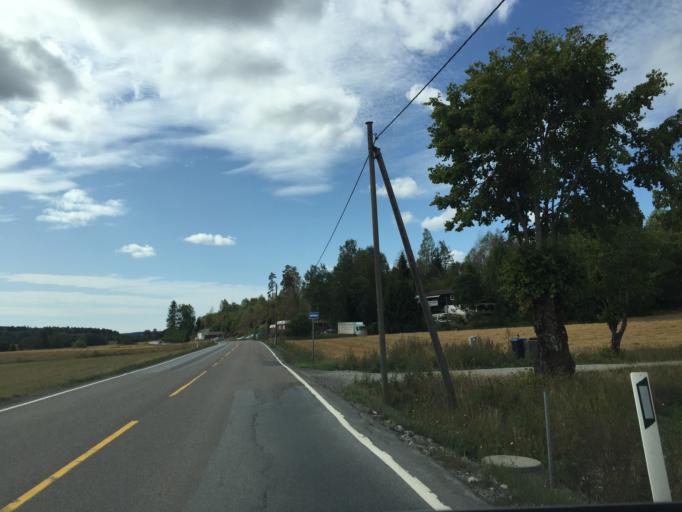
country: NO
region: Ostfold
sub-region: Hobol
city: Elvestad
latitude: 59.6160
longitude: 10.9368
